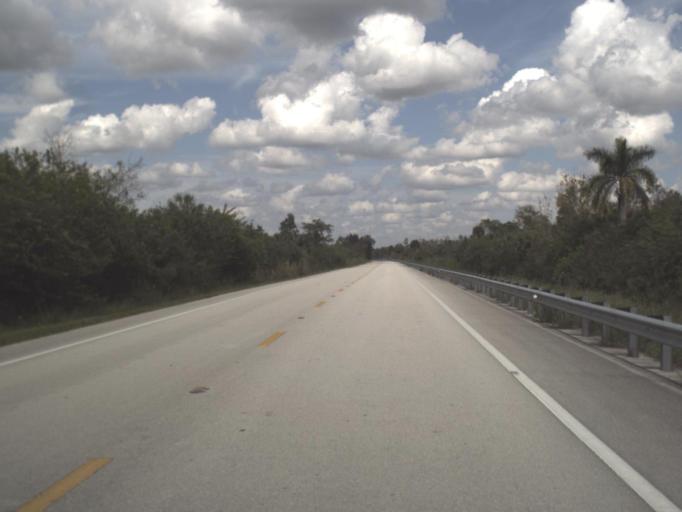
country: US
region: Florida
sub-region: Collier County
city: Lely Resort
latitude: 25.9259
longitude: -81.3579
